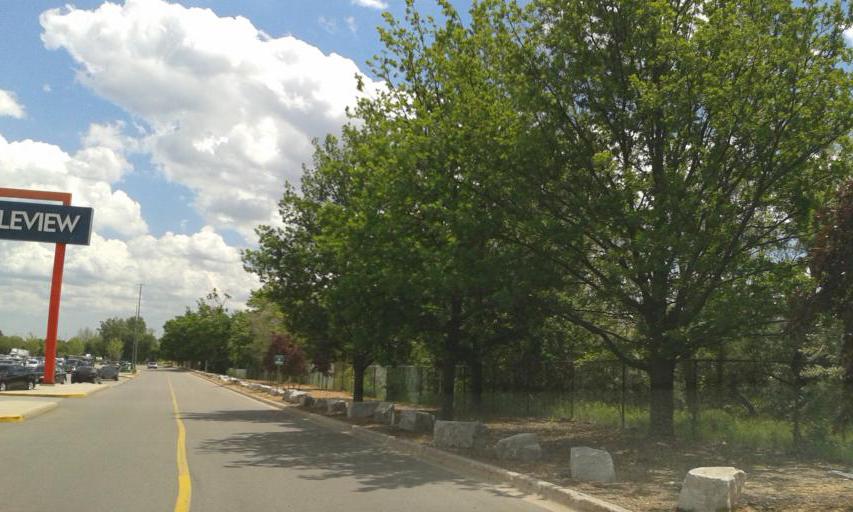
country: CA
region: Ontario
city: Burlington
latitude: 43.3256
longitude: -79.8220
